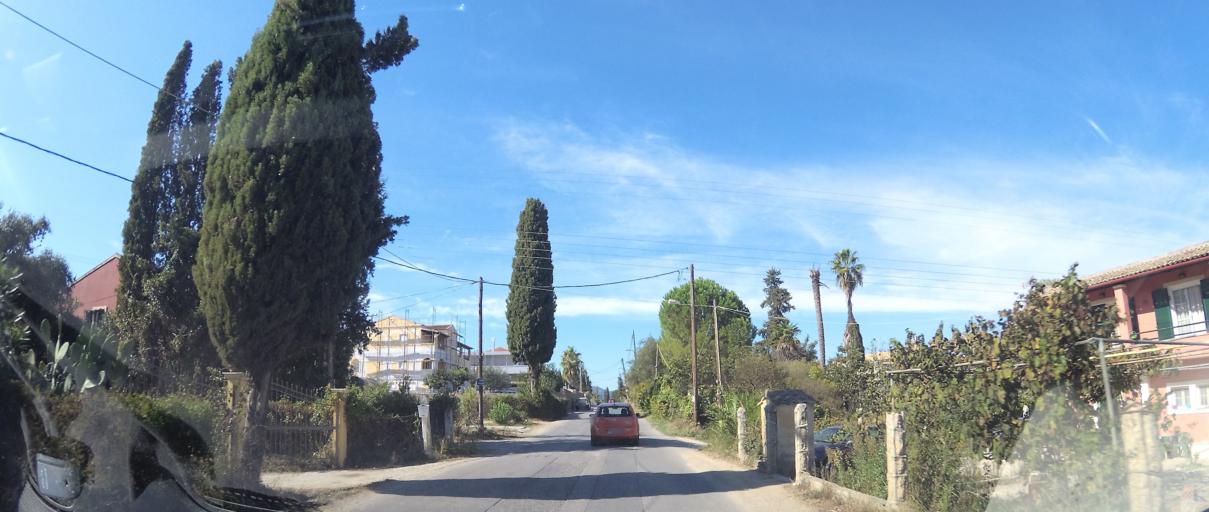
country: GR
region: Ionian Islands
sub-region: Nomos Kerkyras
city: Kontokali
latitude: 39.6464
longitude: 19.8453
